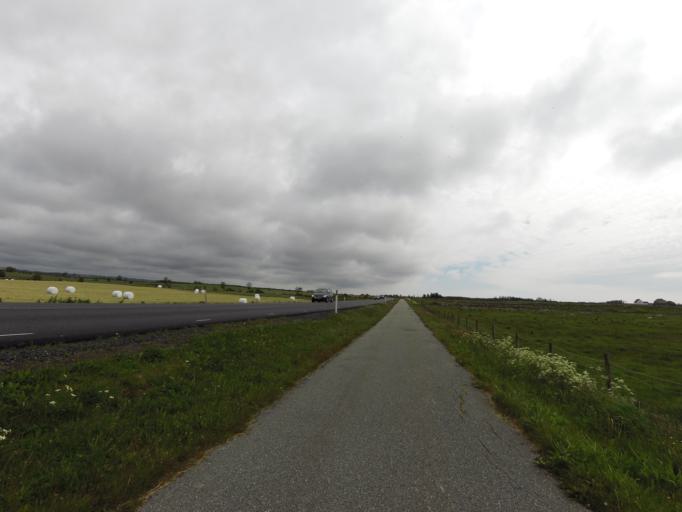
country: NO
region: Rogaland
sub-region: Ha
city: Naerbo
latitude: 58.6474
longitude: 5.6017
